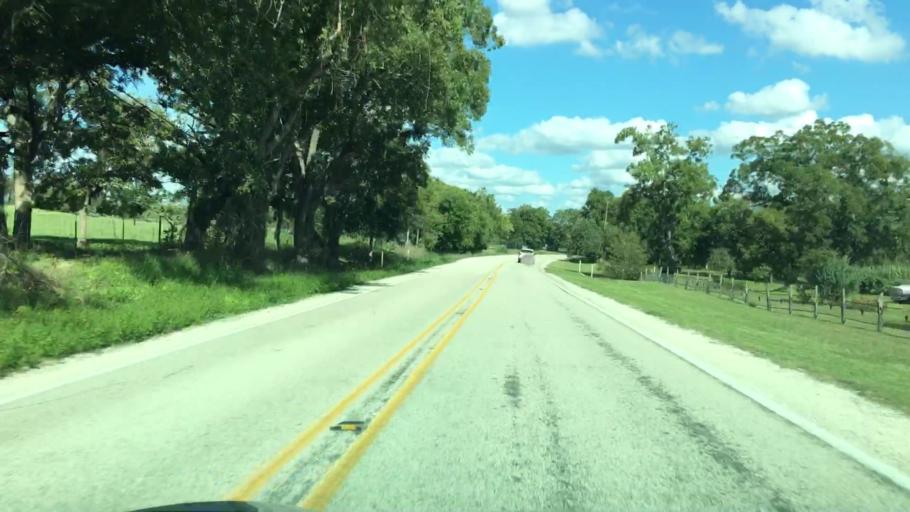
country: US
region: Texas
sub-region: Blanco County
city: Blanco
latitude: 30.0915
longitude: -98.3967
